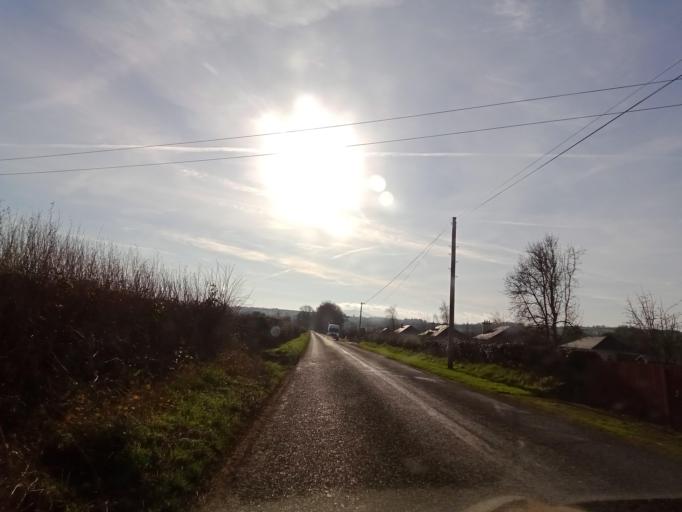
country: IE
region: Munster
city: Fethard
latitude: 52.5687
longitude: -7.5644
